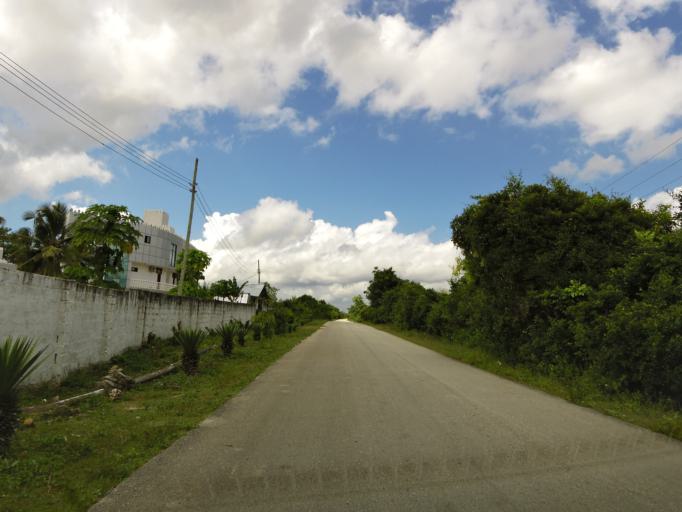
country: TZ
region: Zanzibar Central/South
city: Koani
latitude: -6.1436
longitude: 39.4268
